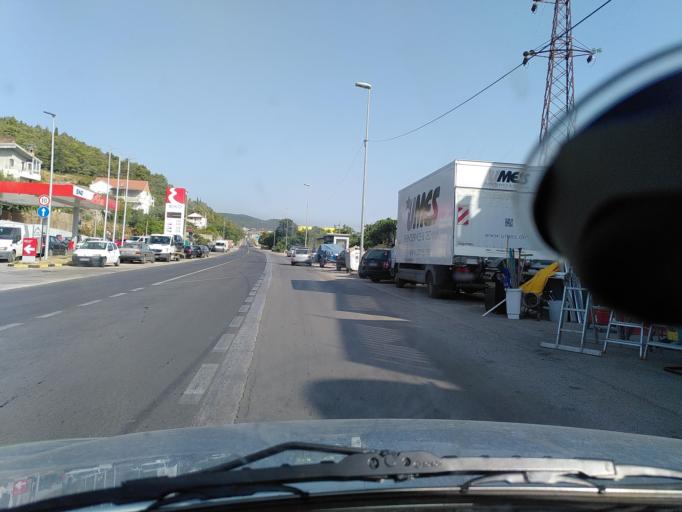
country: ME
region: Ulcinj
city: Ulcinj
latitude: 41.9370
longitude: 19.2193
